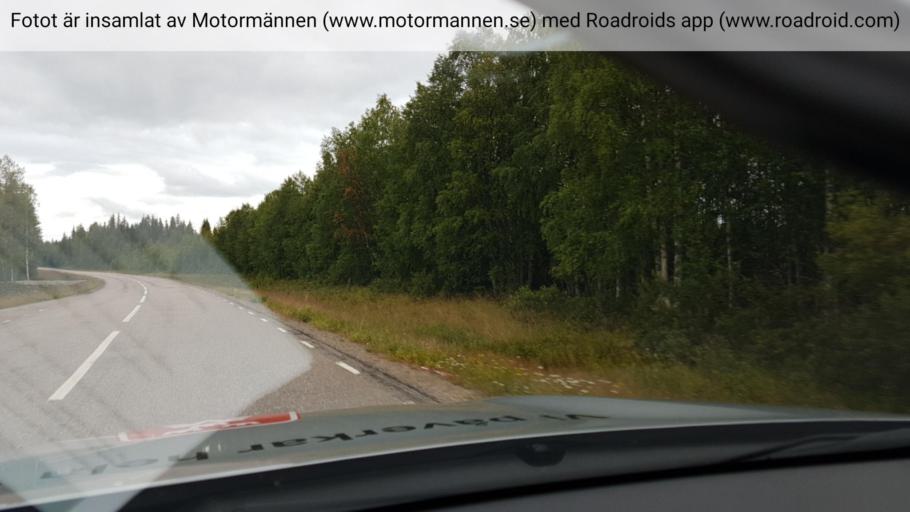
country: SE
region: Norrbotten
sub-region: Overkalix Kommun
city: OEverkalix
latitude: 66.6740
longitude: 22.8468
